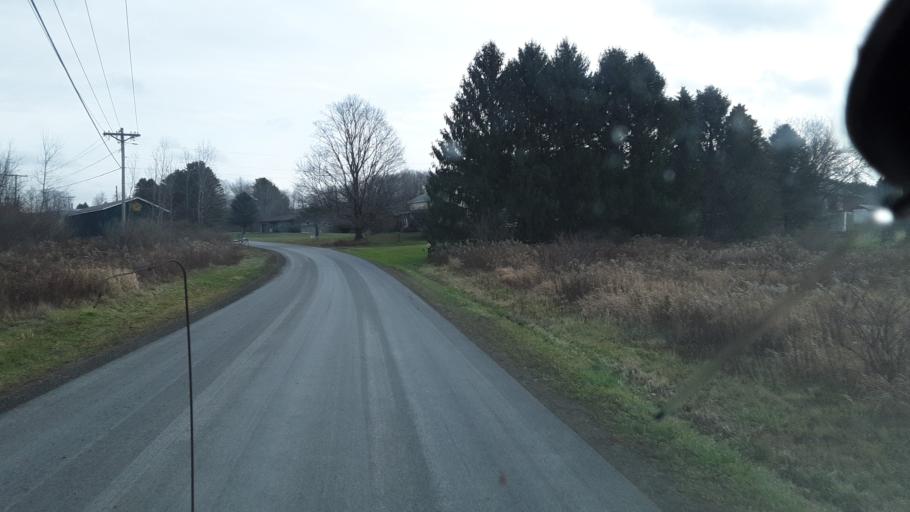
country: US
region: Pennsylvania
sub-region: Potter County
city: Galeton
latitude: 41.8869
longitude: -77.7686
